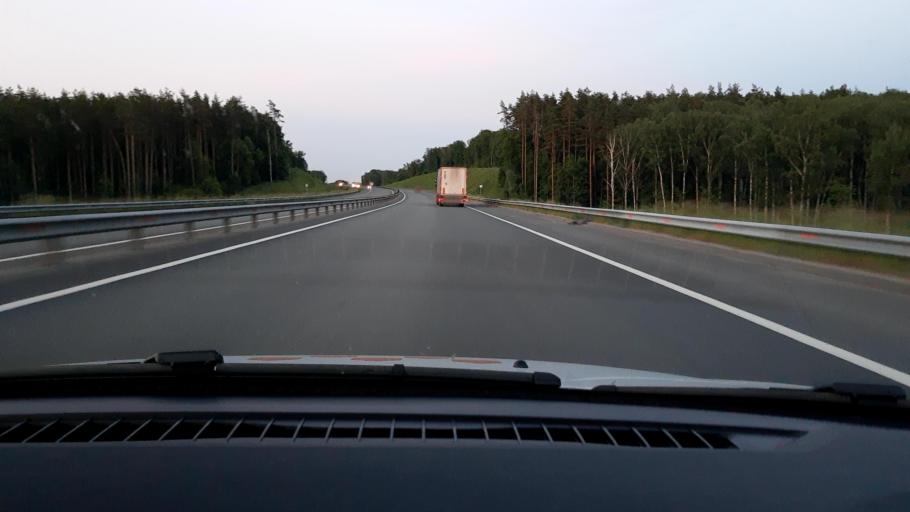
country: RU
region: Nizjnij Novgorod
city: Afonino
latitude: 56.1016
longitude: 44.0200
